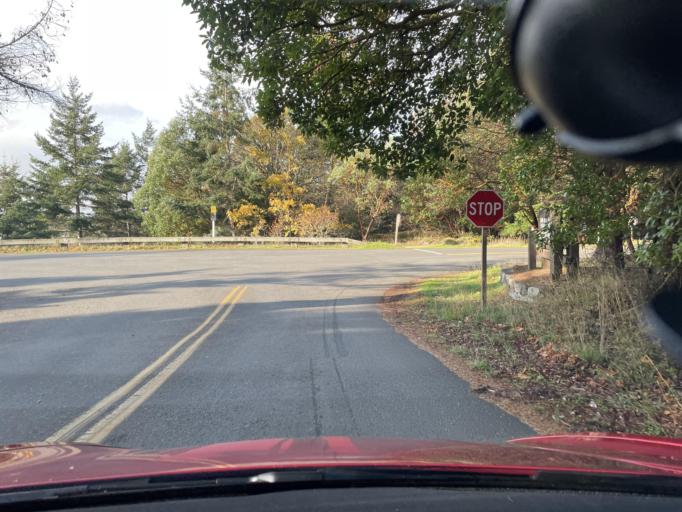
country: US
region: Washington
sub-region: San Juan County
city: Friday Harbor
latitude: 48.5145
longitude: -123.1486
